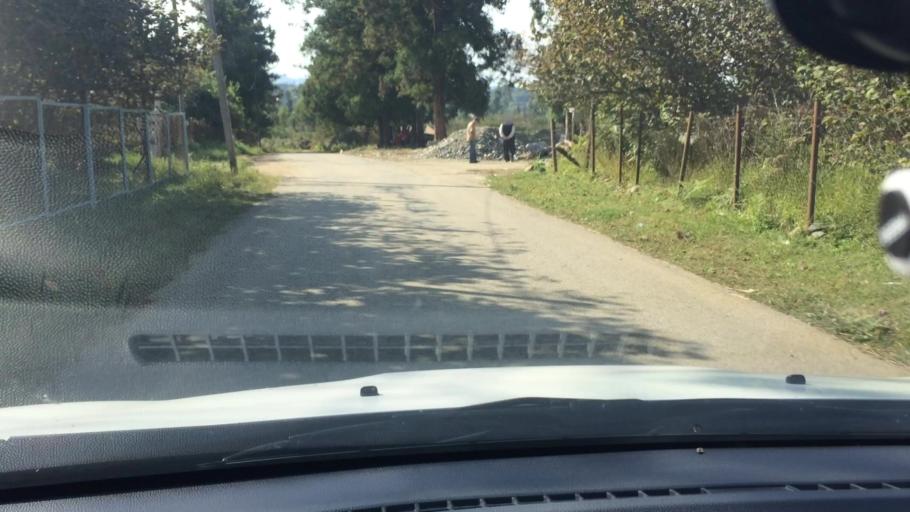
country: GE
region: Ajaria
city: Kobuleti
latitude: 41.8096
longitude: 41.8242
